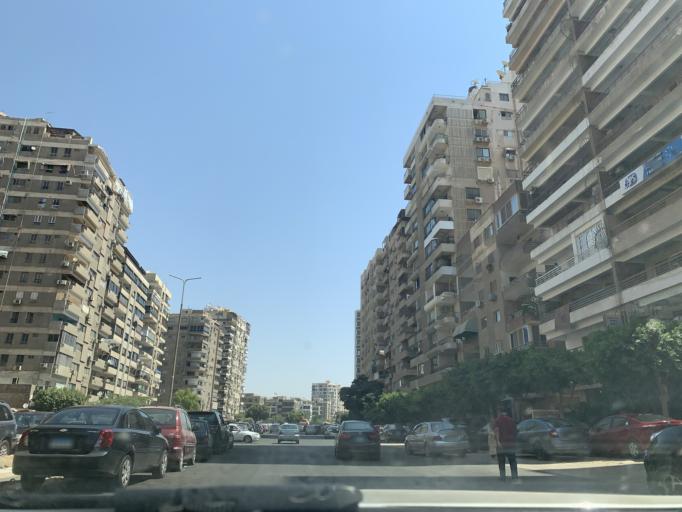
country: EG
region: Muhafazat al Qahirah
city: Cairo
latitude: 30.0614
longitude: 31.3553
